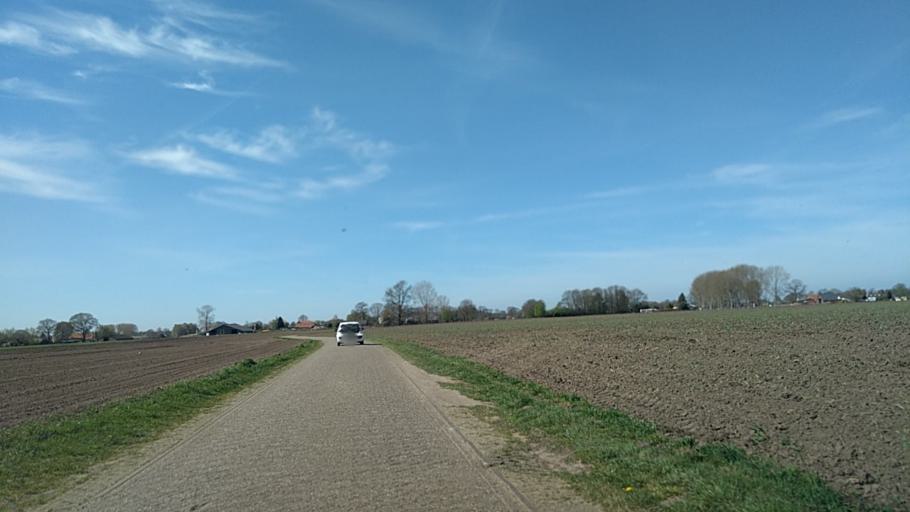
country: NL
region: Gelderland
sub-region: Gemeente Bronckhorst
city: Hengelo
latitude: 52.0210
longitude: 6.3136
